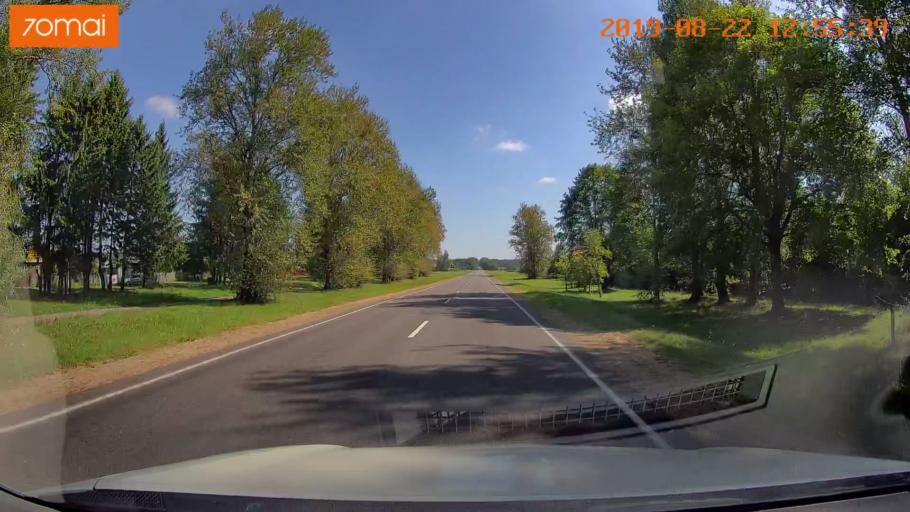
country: BY
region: Minsk
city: Prawdzinski
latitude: 53.4361
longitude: 27.7165
